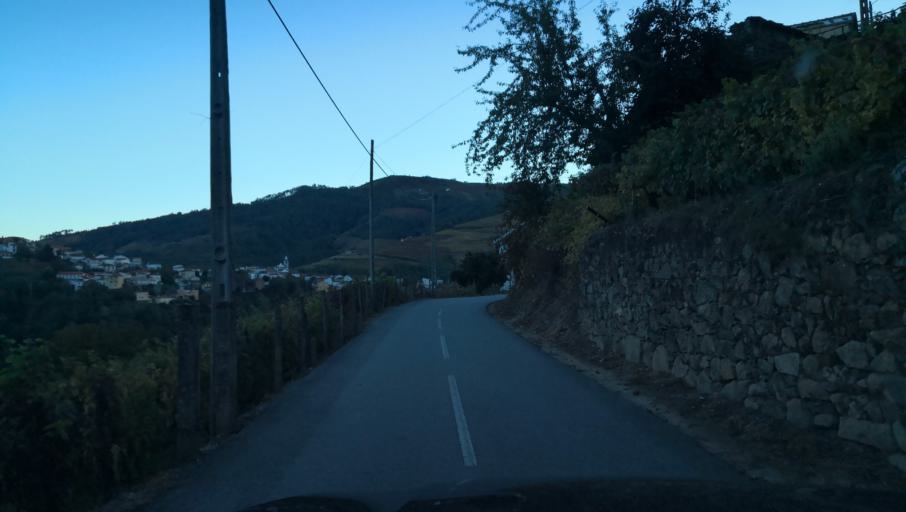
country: PT
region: Vila Real
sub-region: Santa Marta de Penaguiao
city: Santa Marta de Penaguiao
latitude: 41.2532
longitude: -7.8095
